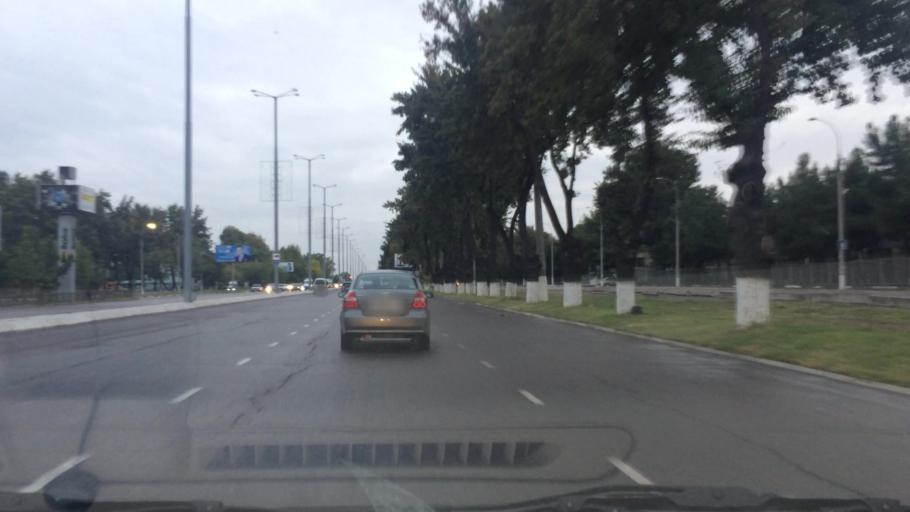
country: UZ
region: Toshkent Shahri
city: Tashkent
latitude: 41.2547
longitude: 69.1901
